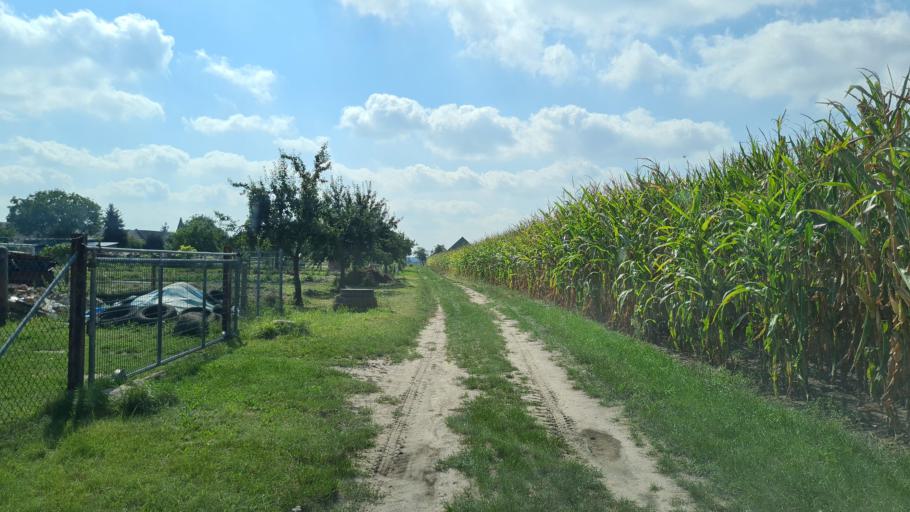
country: DE
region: Brandenburg
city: Sonnewalde
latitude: 51.7333
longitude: 13.6249
